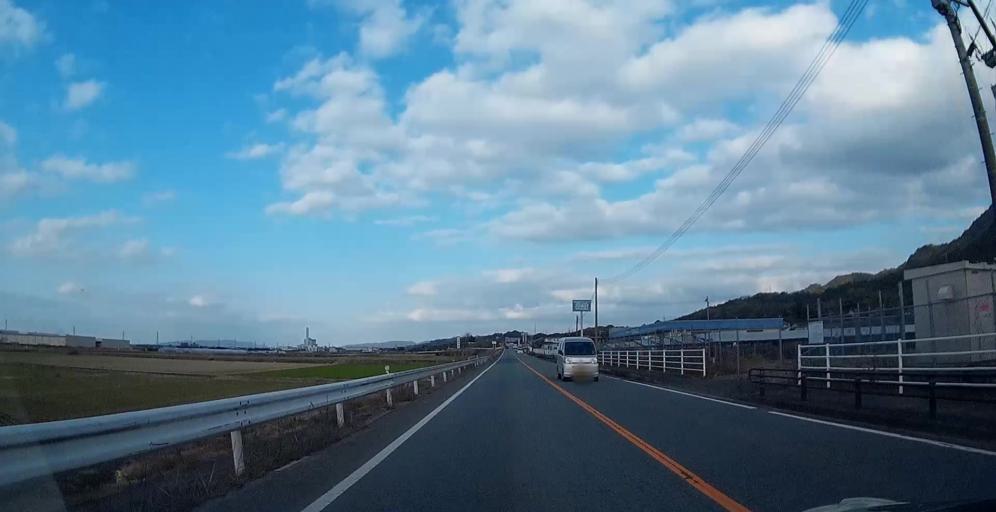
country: JP
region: Kumamoto
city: Yatsushiro
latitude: 32.5339
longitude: 130.6664
